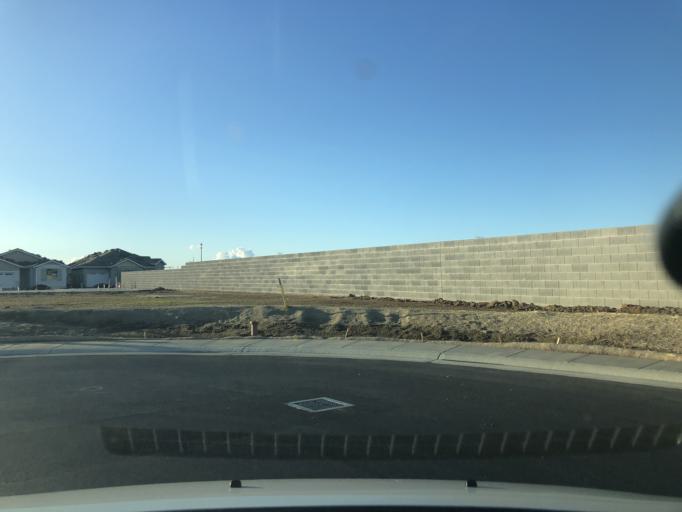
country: US
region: California
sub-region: Sacramento County
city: Antelope
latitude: 38.7605
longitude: -121.3670
